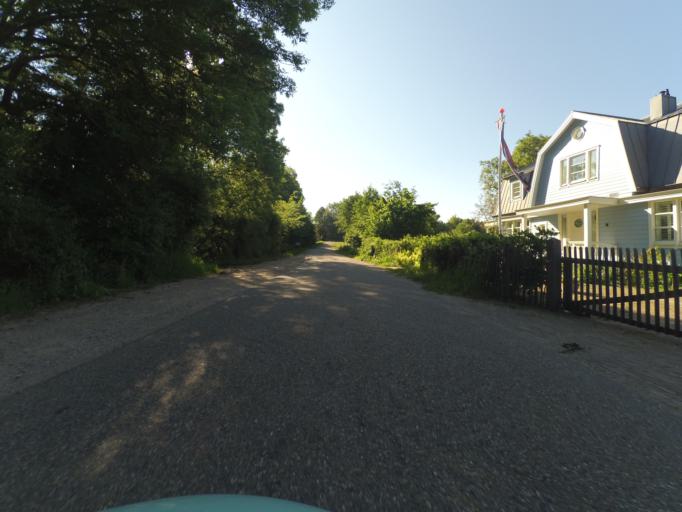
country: NL
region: Gelderland
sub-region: Gemeente Zutphen
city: Zutphen
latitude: 52.1562
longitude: 6.1774
